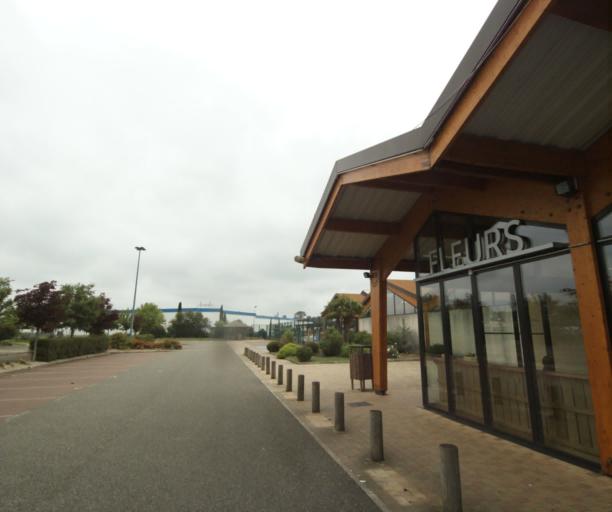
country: FR
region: Midi-Pyrenees
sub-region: Departement du Tarn-et-Garonne
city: Bressols
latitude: 43.9836
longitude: 1.3318
